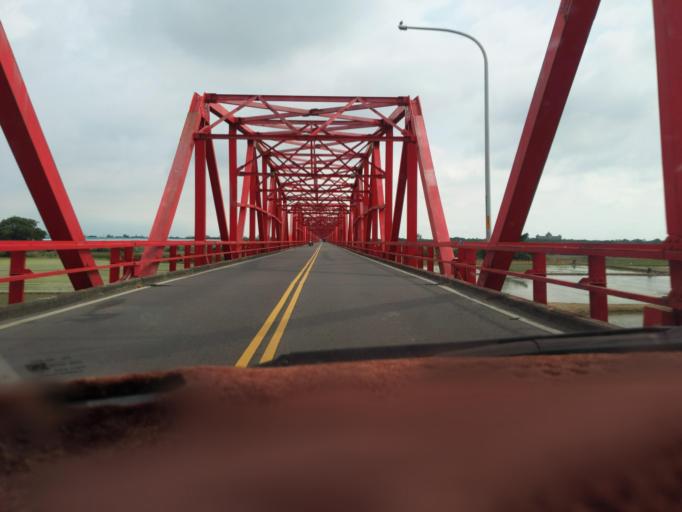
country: TW
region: Taiwan
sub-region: Yunlin
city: Douliu
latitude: 23.8173
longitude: 120.4619
